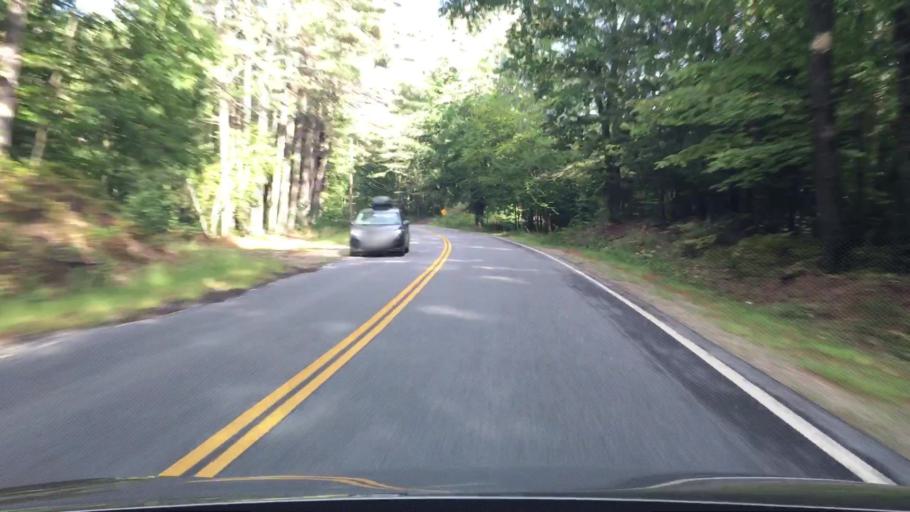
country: US
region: Maine
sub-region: Oxford County
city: Fryeburg
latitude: 44.0289
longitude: -70.9110
